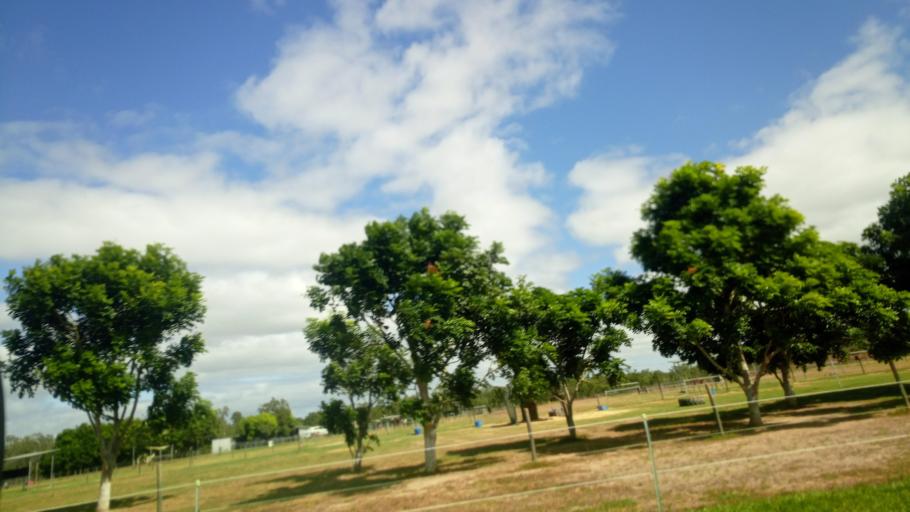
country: AU
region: Queensland
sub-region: Tablelands
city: Mareeba
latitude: -16.9721
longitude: 145.4577
